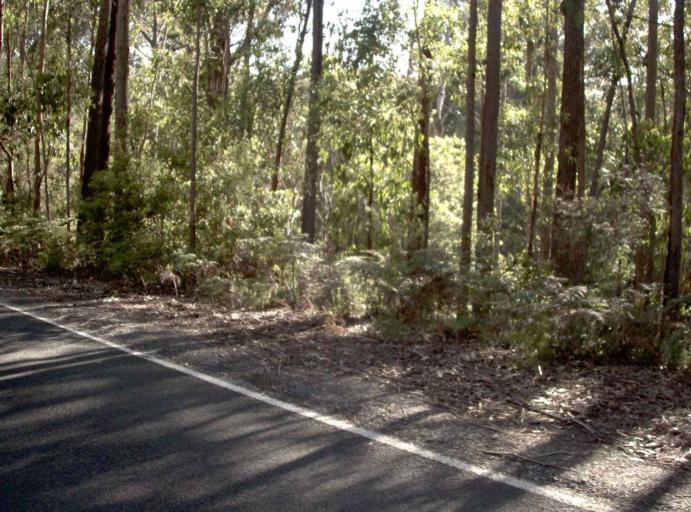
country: AU
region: Victoria
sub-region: East Gippsland
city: Lakes Entrance
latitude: -37.6508
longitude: 148.4794
